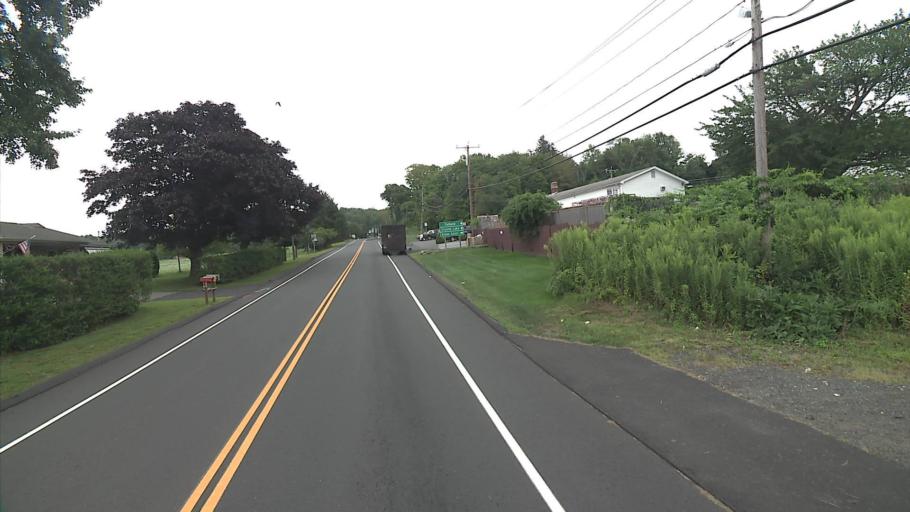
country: US
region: Connecticut
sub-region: Tolland County
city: Tolland
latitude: 41.8711
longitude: -72.4086
